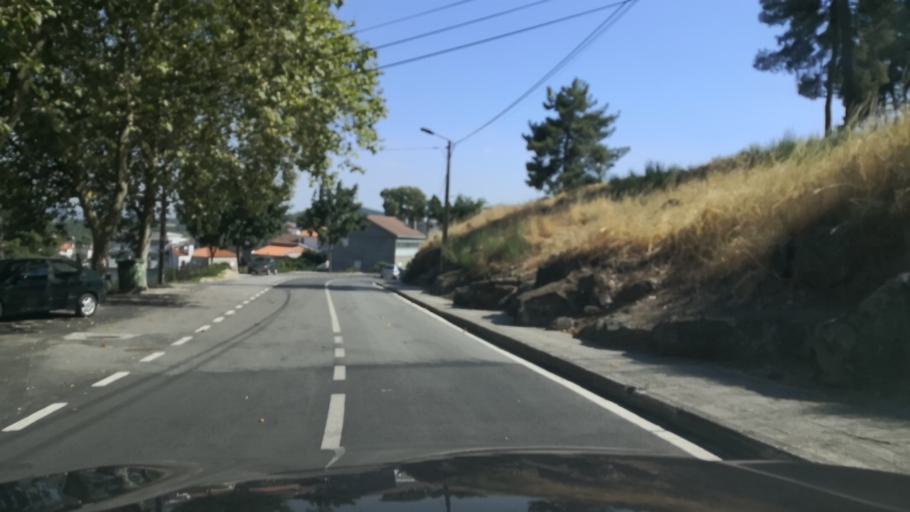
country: PT
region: Vila Real
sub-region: Sabrosa
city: Sabrosa
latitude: 41.2803
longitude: -7.4765
